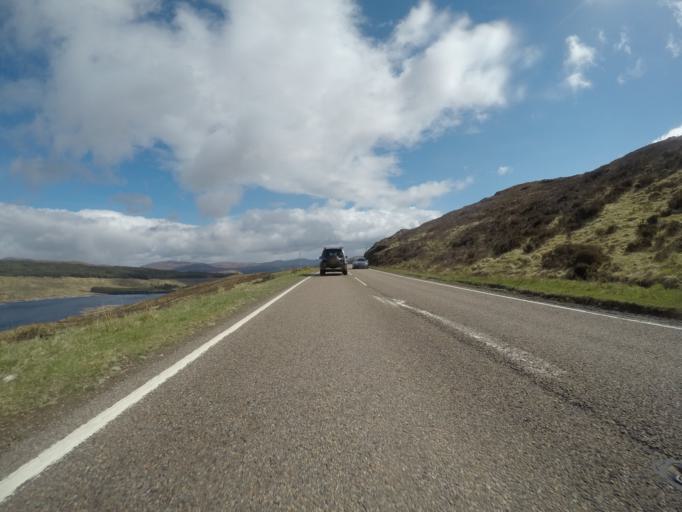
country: GB
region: Scotland
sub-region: Highland
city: Spean Bridge
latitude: 57.1196
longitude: -4.9776
